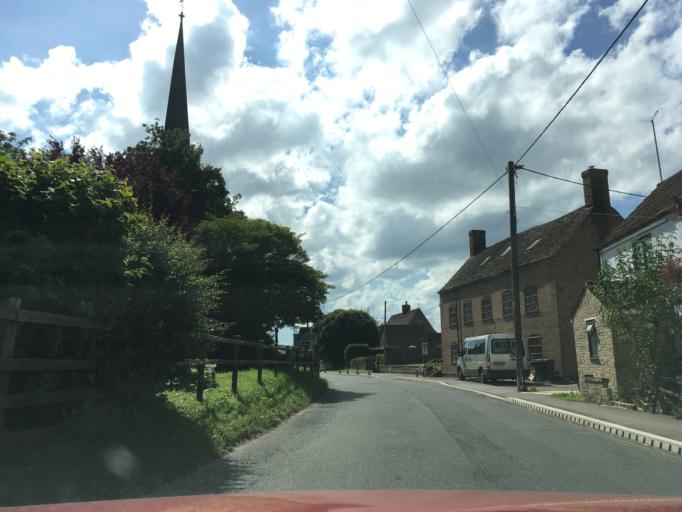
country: GB
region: England
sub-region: Gloucestershire
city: Dursley
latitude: 51.7306
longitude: -2.3783
